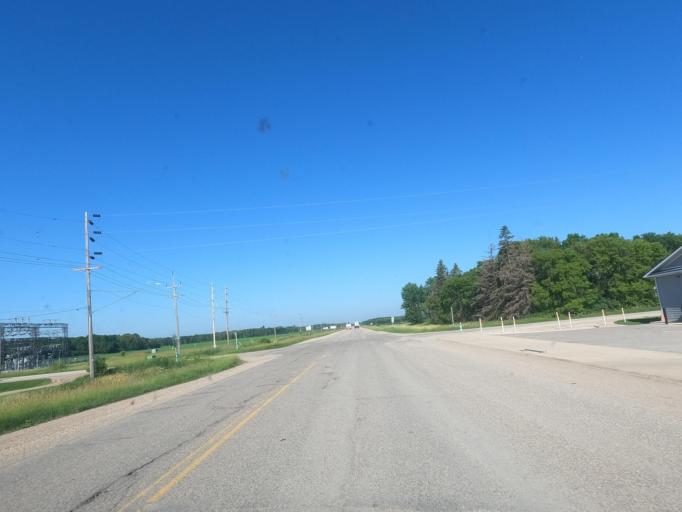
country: CA
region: Manitoba
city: Portage la Prairie
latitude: 49.6652
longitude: -98.3459
